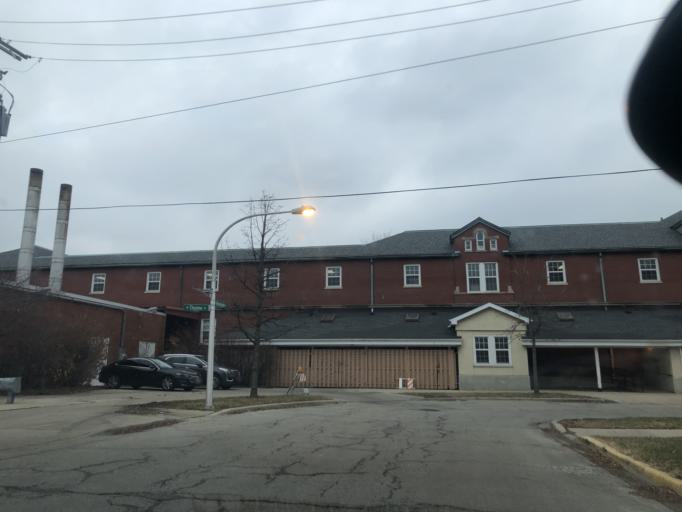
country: US
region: Illinois
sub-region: Cook County
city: Evanston
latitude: 41.9952
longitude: -87.6785
